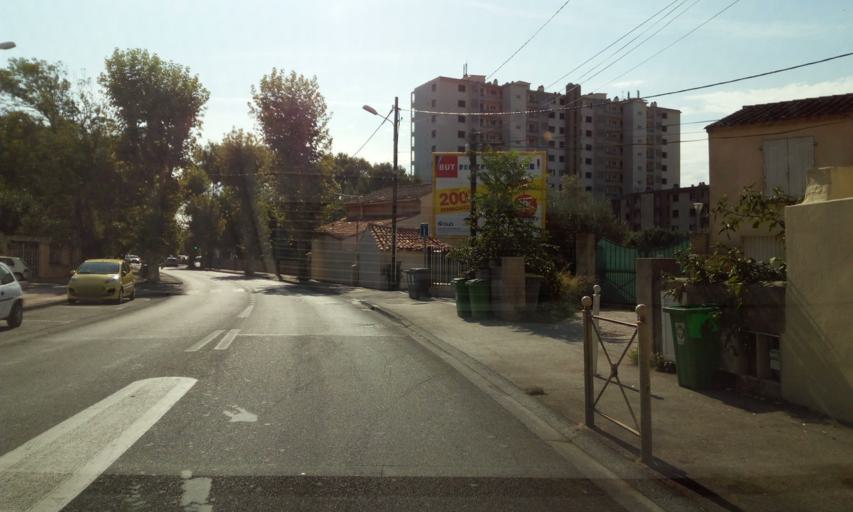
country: FR
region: Provence-Alpes-Cote d'Azur
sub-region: Departement du Var
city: La Valette-du-Var
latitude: 43.1229
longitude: 5.9710
